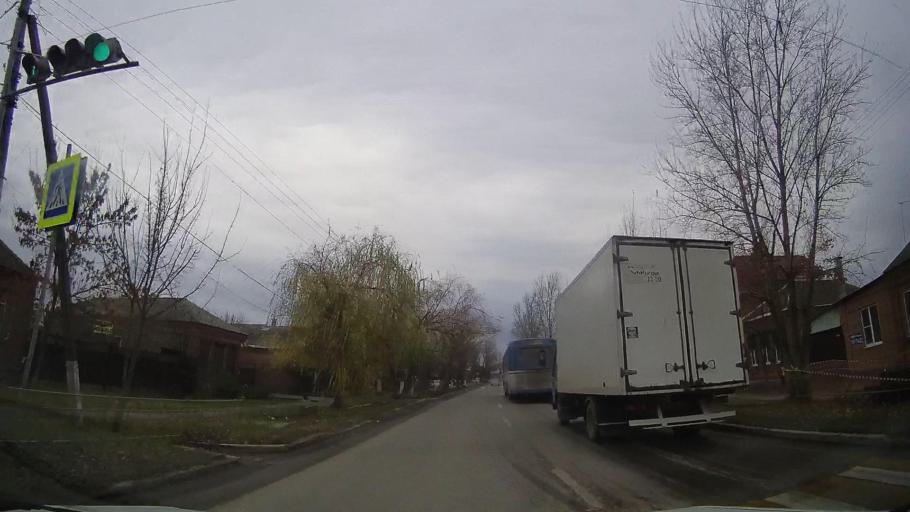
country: RU
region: Rostov
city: Bataysk
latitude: 47.1292
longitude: 39.7435
